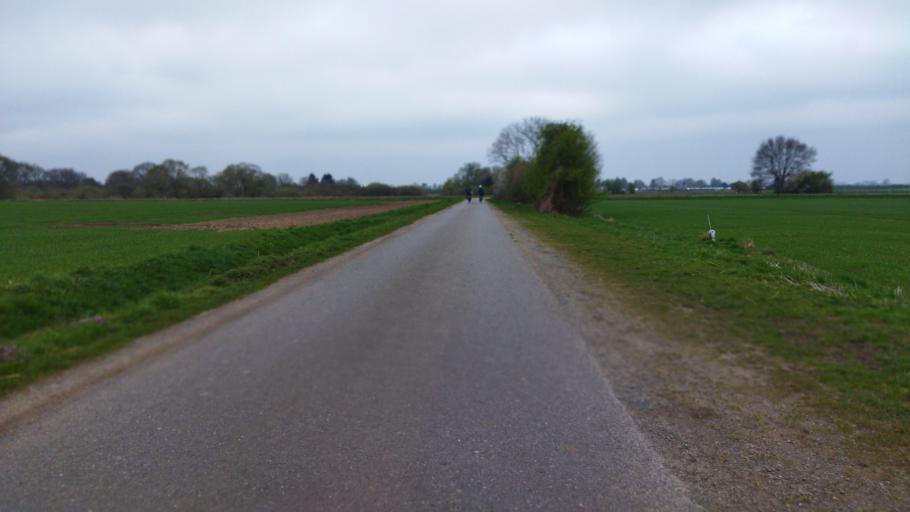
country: DE
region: Lower Saxony
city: Riede
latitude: 53.0110
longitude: 8.9646
